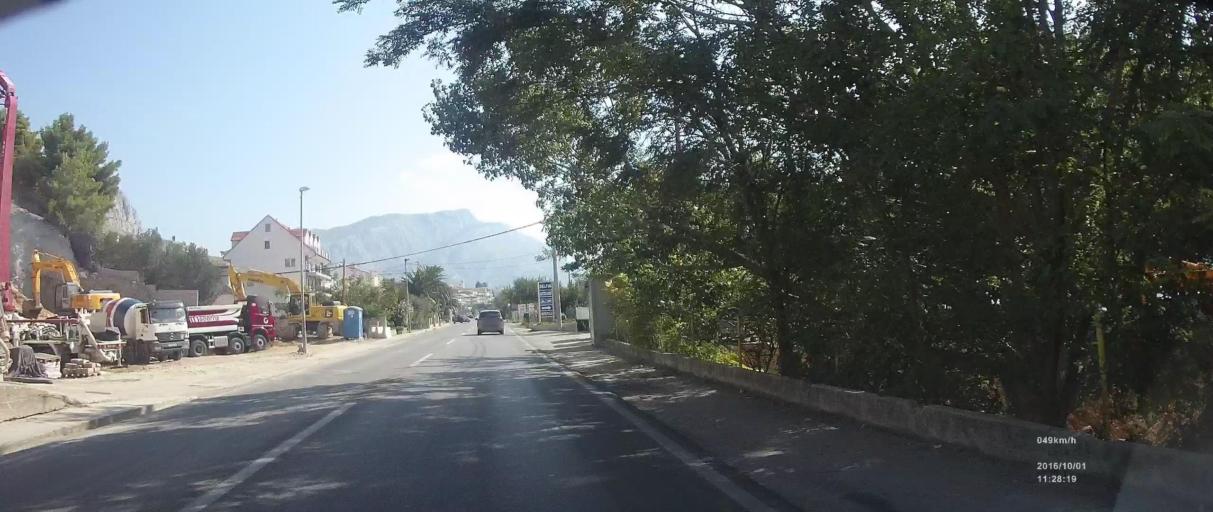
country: HR
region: Splitsko-Dalmatinska
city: Duce
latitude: 43.4413
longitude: 16.6568
